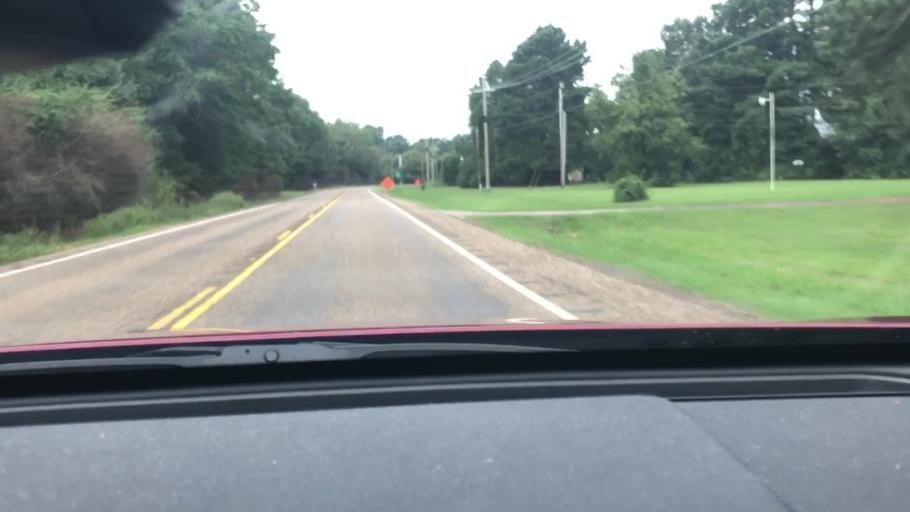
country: US
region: Texas
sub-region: Bowie County
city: Wake Village
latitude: 33.3821
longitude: -94.1054
